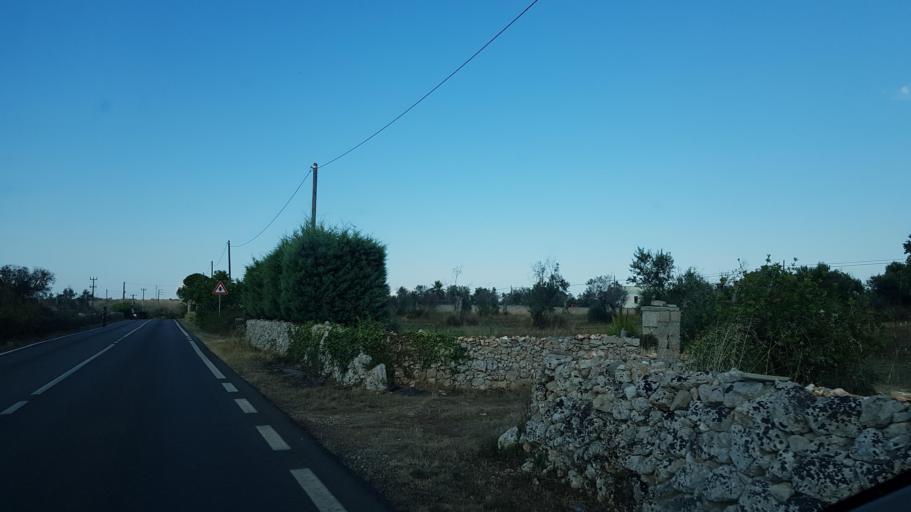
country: IT
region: Apulia
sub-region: Provincia di Lecce
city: Castiglione
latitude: 39.9838
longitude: 18.3540
